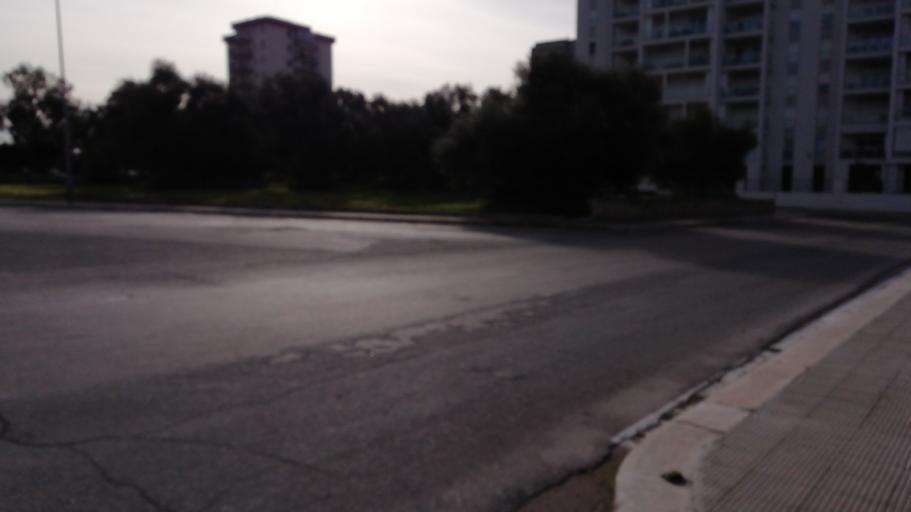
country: IT
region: Apulia
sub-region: Provincia di Bari
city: Triggiano
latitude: 41.1031
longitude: 16.9159
